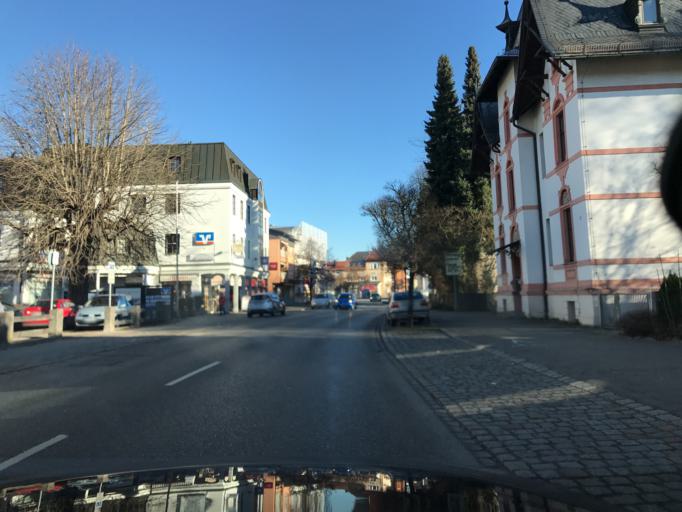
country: DE
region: Bavaria
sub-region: Upper Bavaria
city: Rosenheim
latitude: 47.8577
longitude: 12.1459
